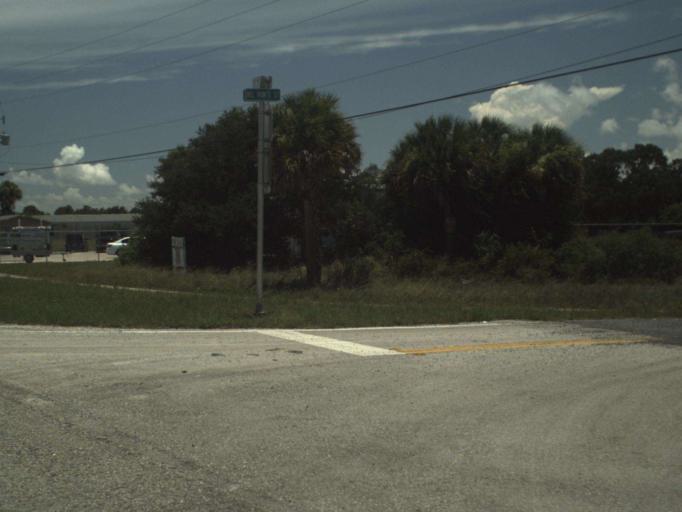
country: US
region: Florida
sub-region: Saint Lucie County
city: Lakewood Park
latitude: 27.5192
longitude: -80.3551
